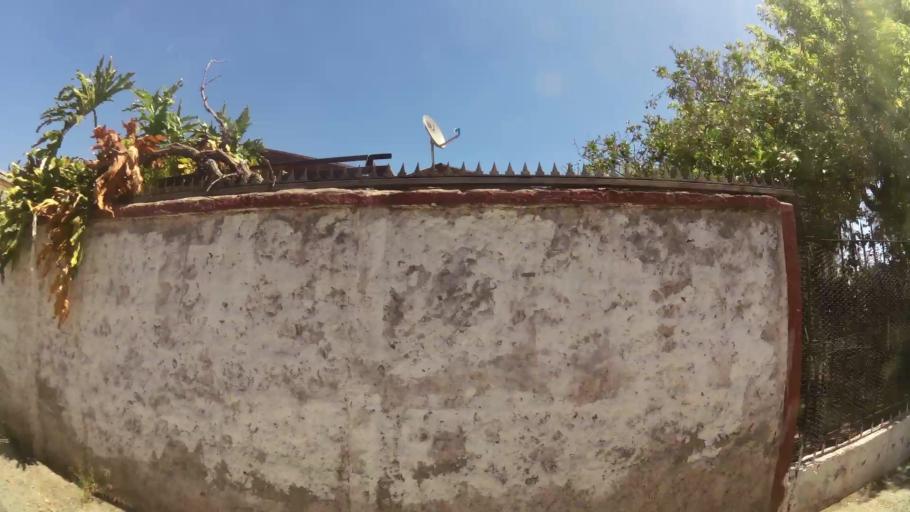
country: CL
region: Santiago Metropolitan
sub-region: Provincia de Maipo
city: San Bernardo
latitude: -33.5728
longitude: -70.6870
